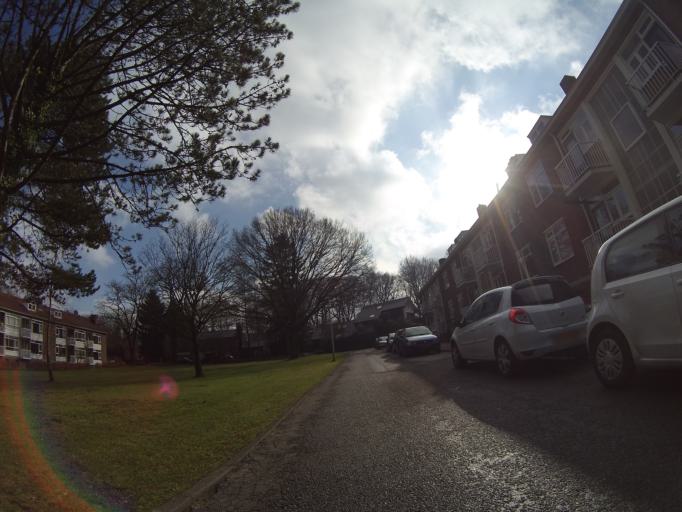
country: NL
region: Utrecht
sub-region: Gemeente Amersfoort
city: Amersfoort
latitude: 52.1469
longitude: 5.3580
